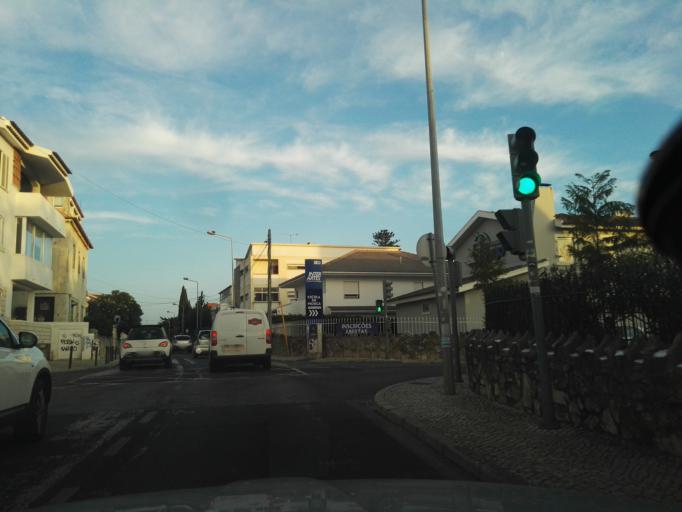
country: PT
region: Lisbon
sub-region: Cascais
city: Estoril
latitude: 38.7004
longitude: -9.3875
